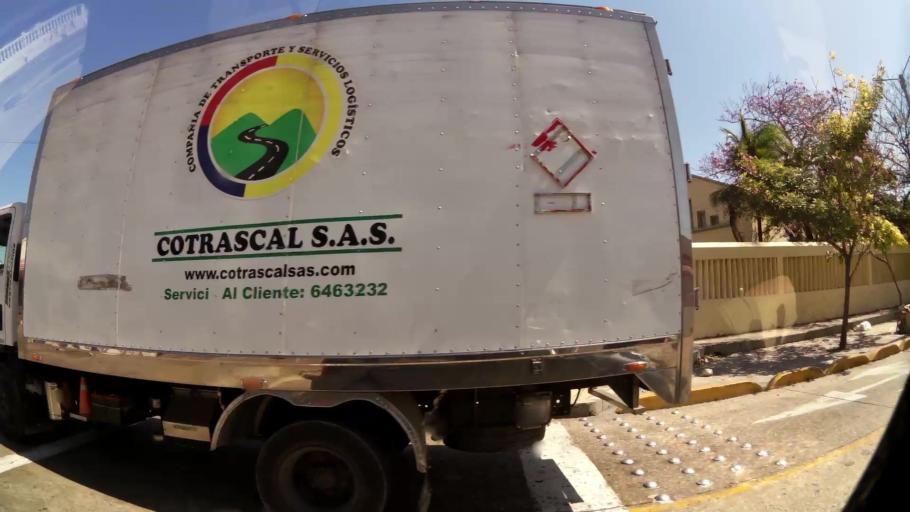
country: CO
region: Atlantico
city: Barranquilla
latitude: 11.0036
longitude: -74.7951
